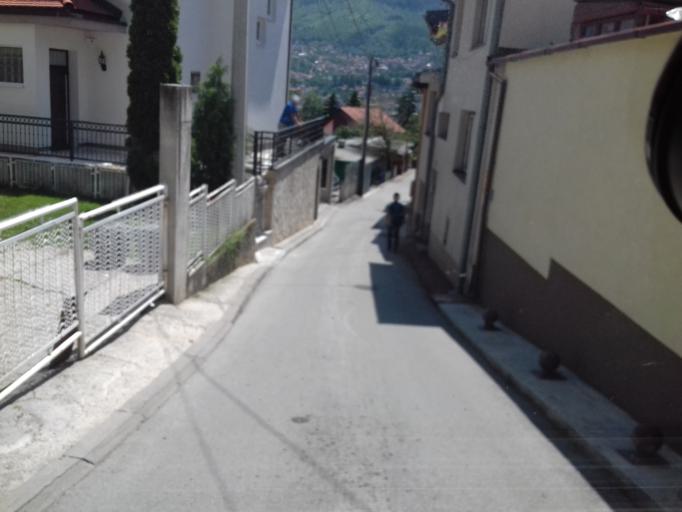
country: BA
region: Federation of Bosnia and Herzegovina
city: Kobilja Glava
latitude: 43.8660
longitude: 18.4237
